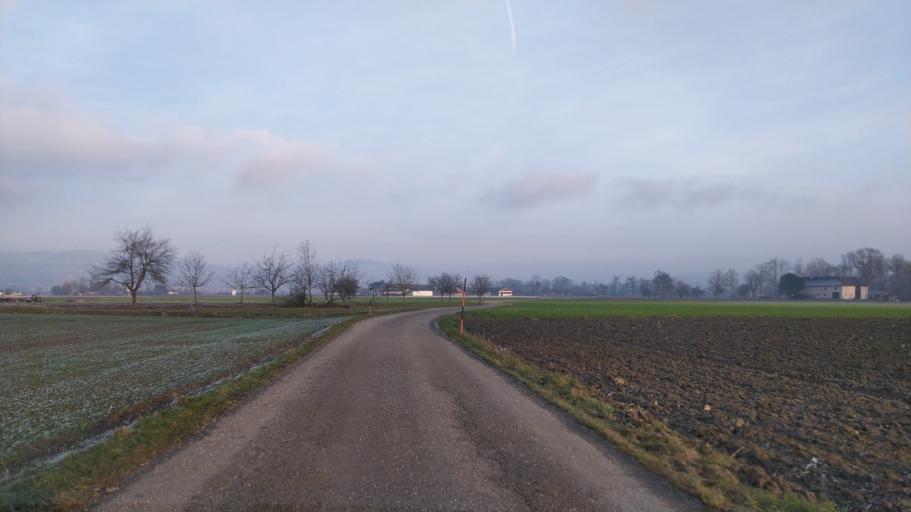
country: AT
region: Upper Austria
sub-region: Politischer Bezirk Urfahr-Umgebung
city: Goldworth
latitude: 48.3283
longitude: 14.1186
